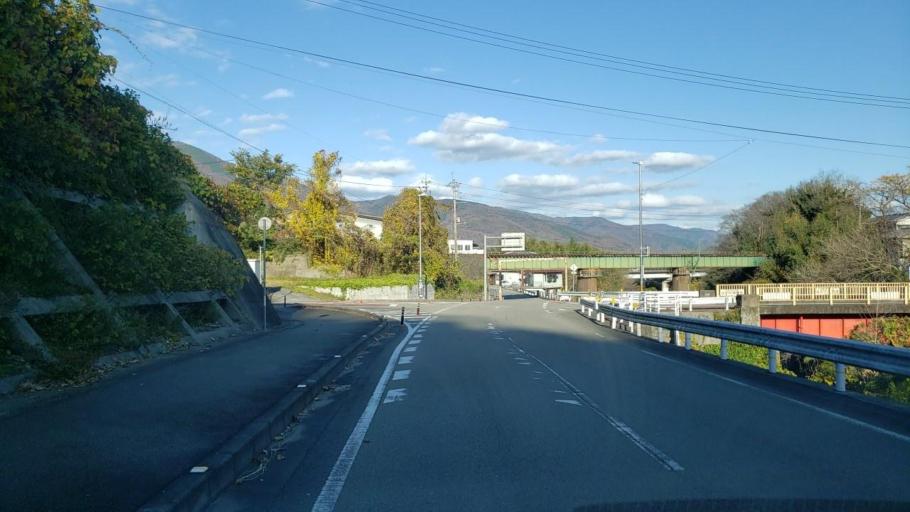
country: JP
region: Tokushima
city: Wakimachi
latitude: 34.0405
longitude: 134.0276
